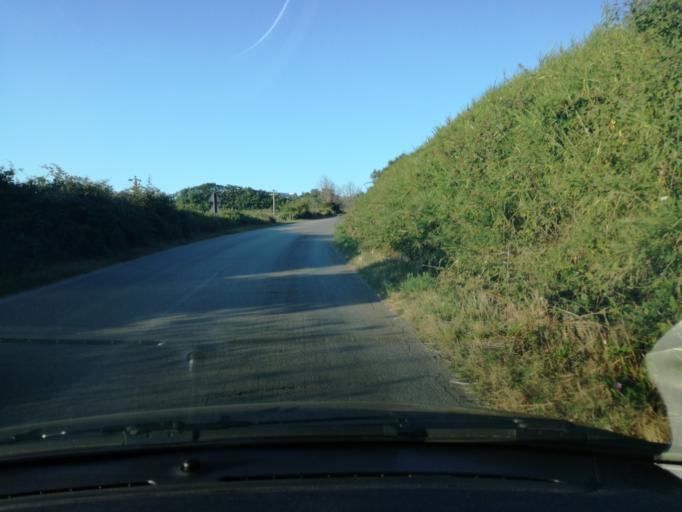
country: IT
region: Molise
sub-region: Provincia di Campobasso
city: San Giacomo degli Schiavoni
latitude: 41.9337
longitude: 14.9420
